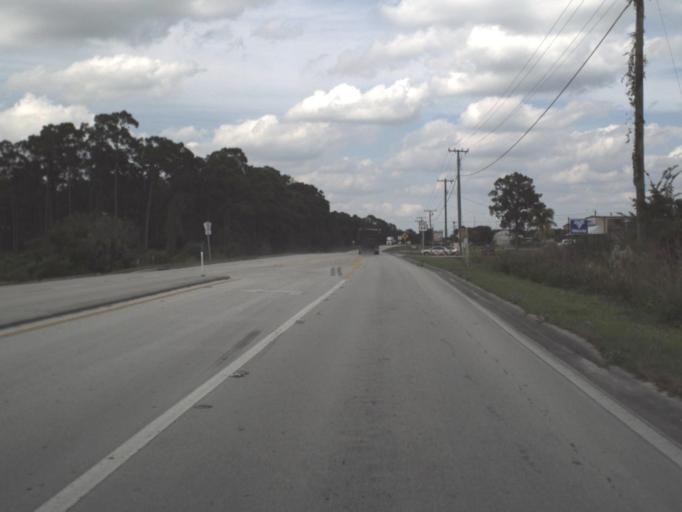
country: US
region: Florida
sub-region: Okeechobee County
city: Cypress Quarters
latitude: 27.2794
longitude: -80.8288
